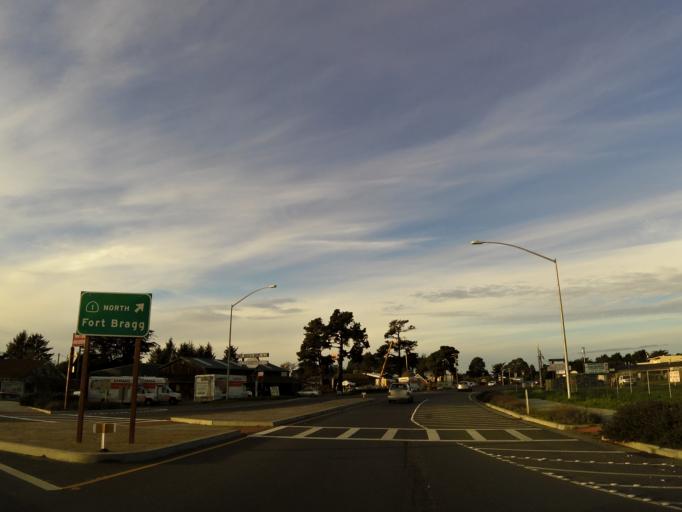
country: US
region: California
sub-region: Mendocino County
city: Fort Bragg
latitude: 39.4125
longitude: -123.8082
